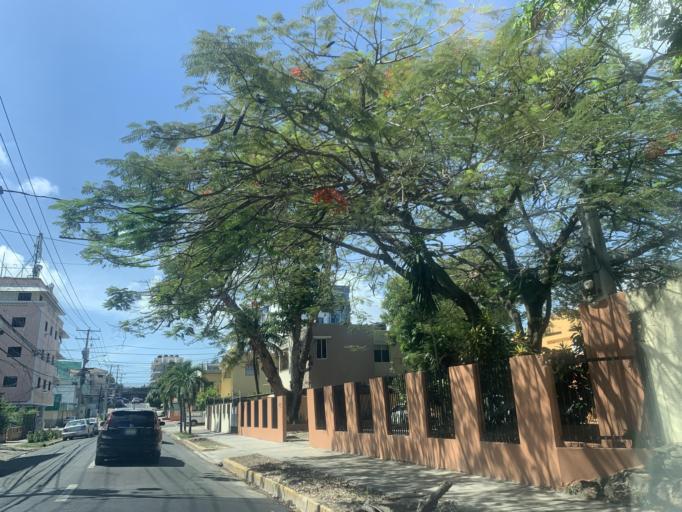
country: DO
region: Nacional
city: San Carlos
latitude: 18.4754
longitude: -69.9026
